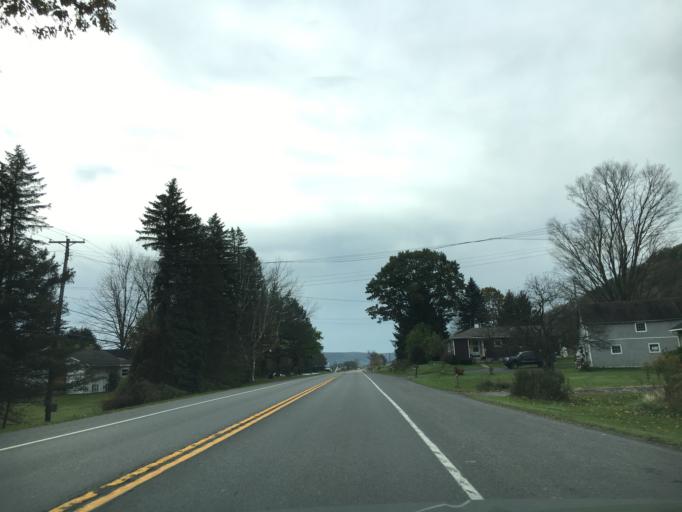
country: US
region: New York
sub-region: Otsego County
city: Cooperstown
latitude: 42.5834
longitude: -74.9482
